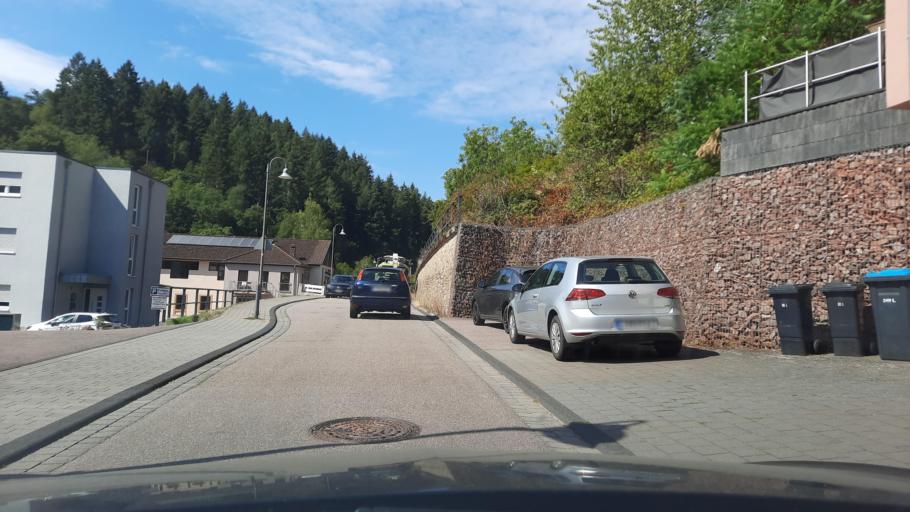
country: DE
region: Rheinland-Pfalz
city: Saarburg
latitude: 49.6100
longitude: 6.5437
